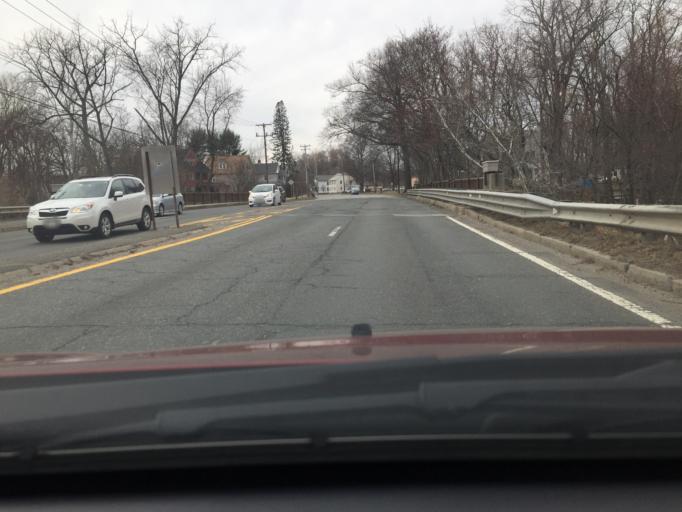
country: US
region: Massachusetts
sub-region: Hampden County
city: Westfield
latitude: 42.1163
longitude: -72.7331
